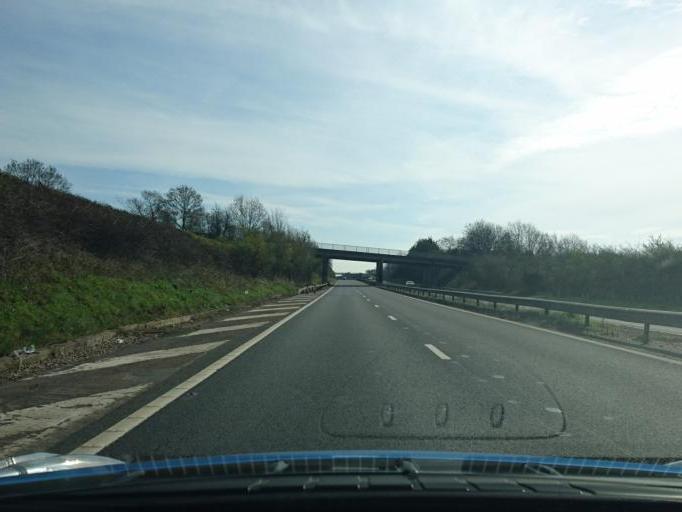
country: GB
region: England
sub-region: Herefordshire
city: Donnington
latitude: 51.9955
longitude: -2.3202
